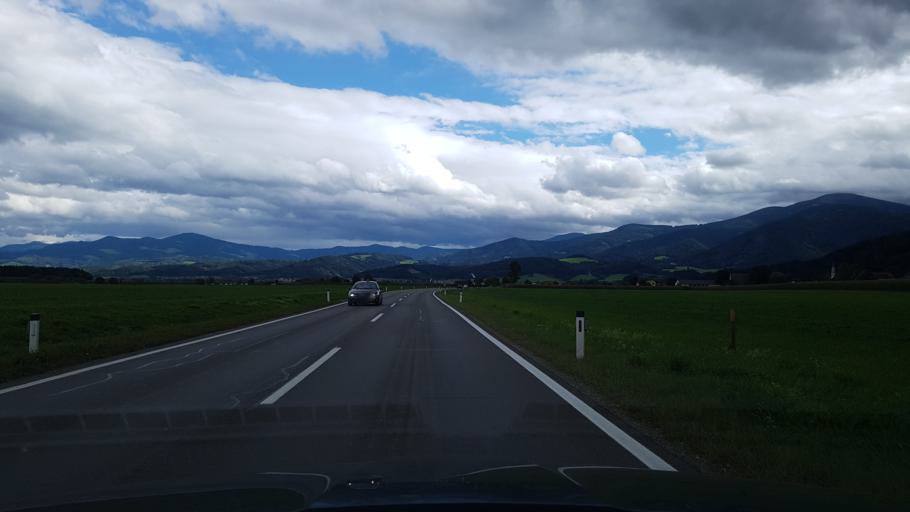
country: AT
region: Styria
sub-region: Politischer Bezirk Murtal
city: Judenburg
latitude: 47.1666
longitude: 14.6887
